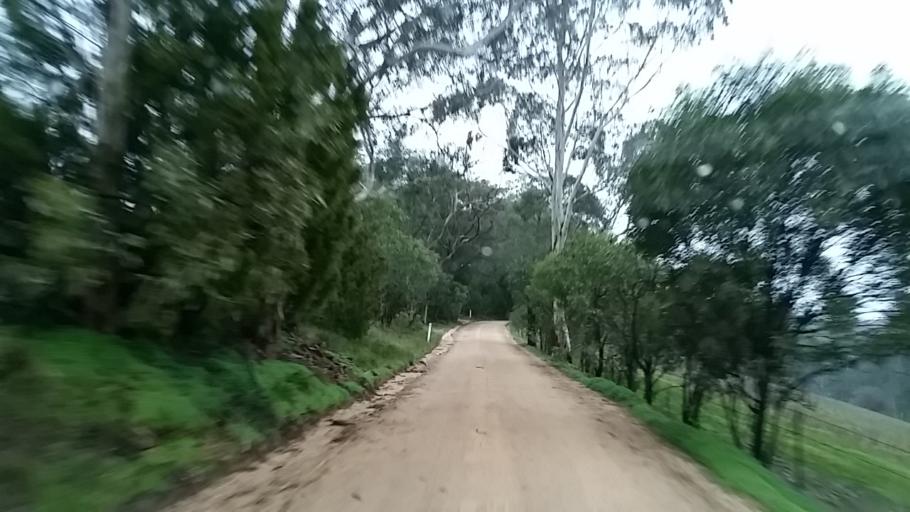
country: AU
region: South Australia
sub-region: Adelaide Hills
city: Adelaide Hills
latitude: -34.9293
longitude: 138.7427
